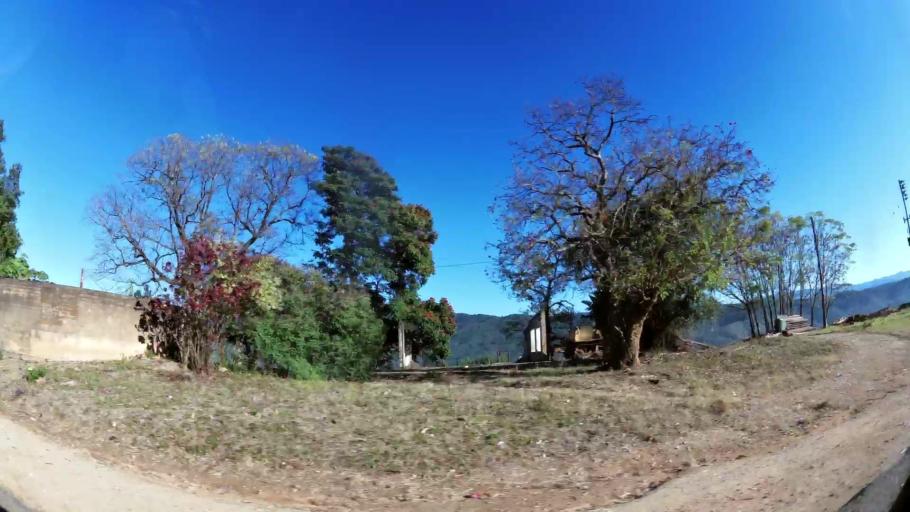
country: ZA
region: Limpopo
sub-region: Mopani District Municipality
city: Tzaneen
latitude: -23.8608
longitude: 30.1093
